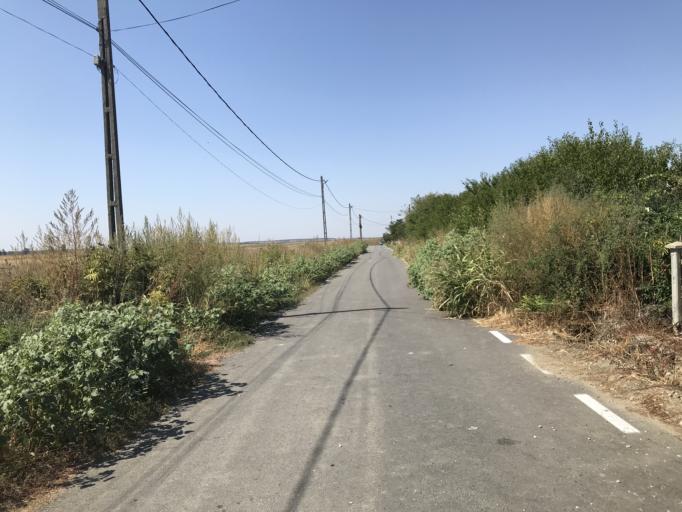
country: RO
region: Olt
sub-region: Comuna Falcoiu
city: Falcoiu
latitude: 44.2439
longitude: 24.3522
